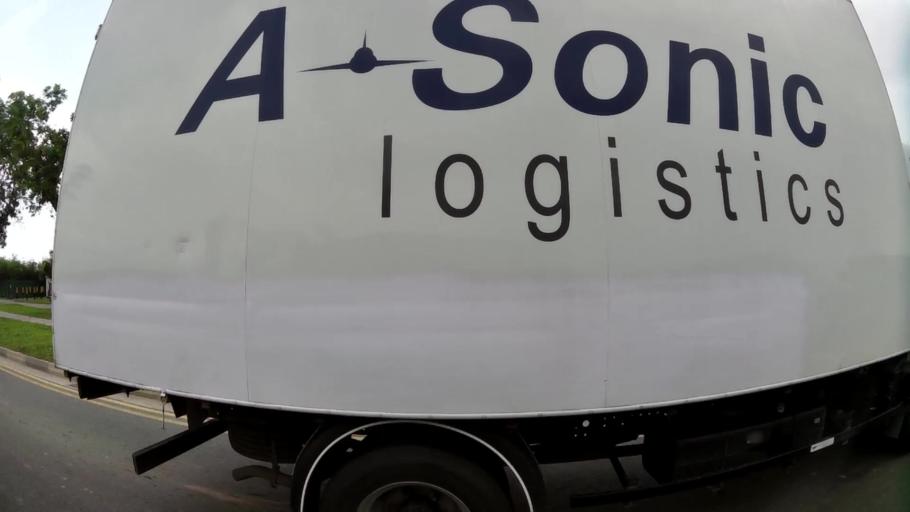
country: SG
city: Singapore
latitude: 1.3326
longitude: 103.9896
